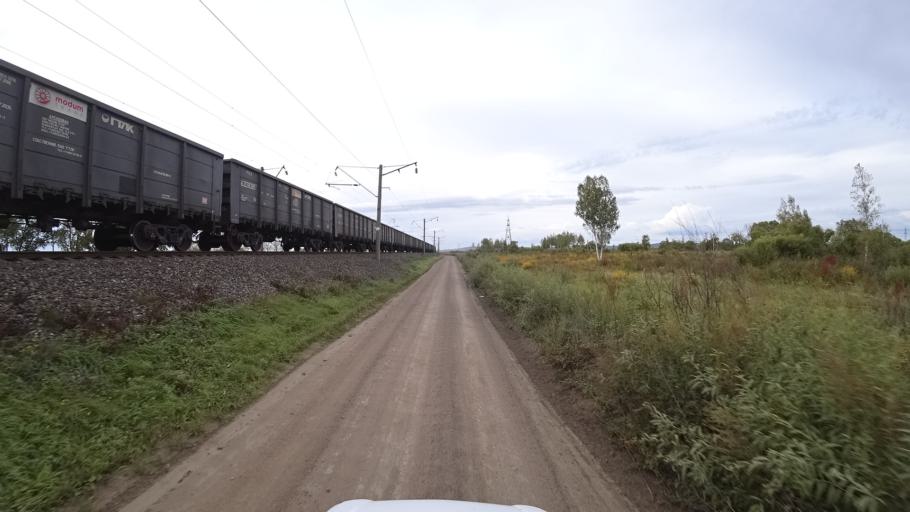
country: RU
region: Amur
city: Arkhara
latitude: 49.3667
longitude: 130.1437
